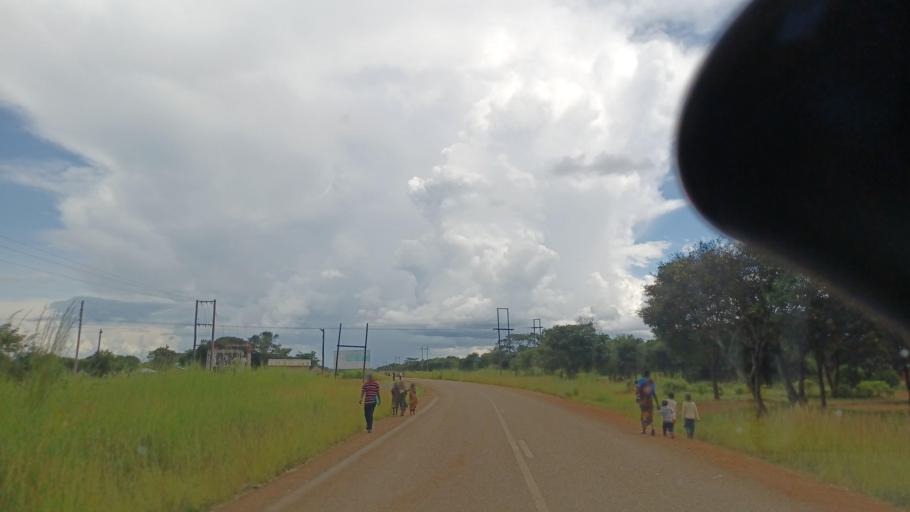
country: ZM
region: North-Western
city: Kasempa
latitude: -13.1119
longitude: 25.8697
